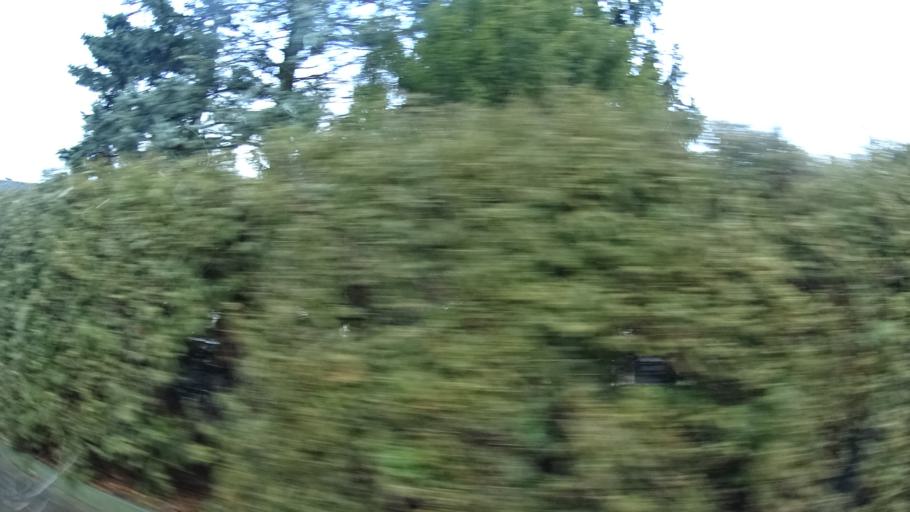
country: DE
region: Hesse
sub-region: Regierungsbezirk Kassel
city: Flieden
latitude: 50.4083
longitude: 9.5728
